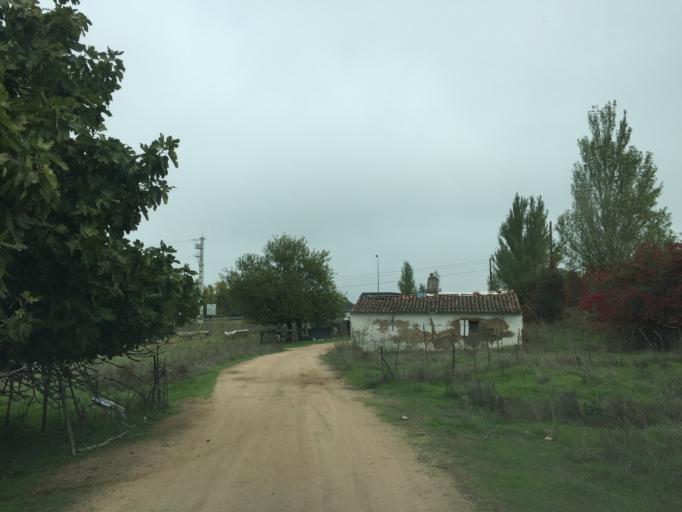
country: PT
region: Portalegre
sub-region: Arronches
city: Arronches
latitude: 39.0550
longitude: -7.4456
